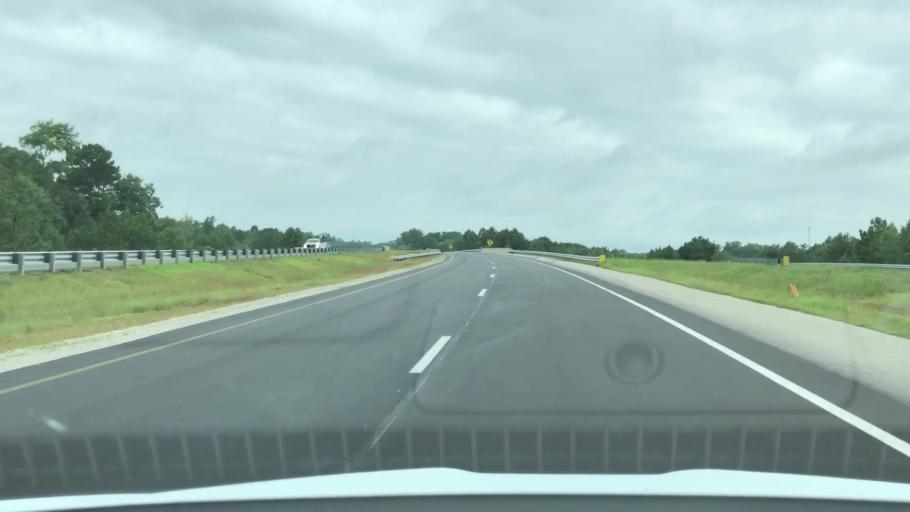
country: US
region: North Carolina
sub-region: Wilson County
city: Lucama
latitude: 35.6656
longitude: -77.9558
